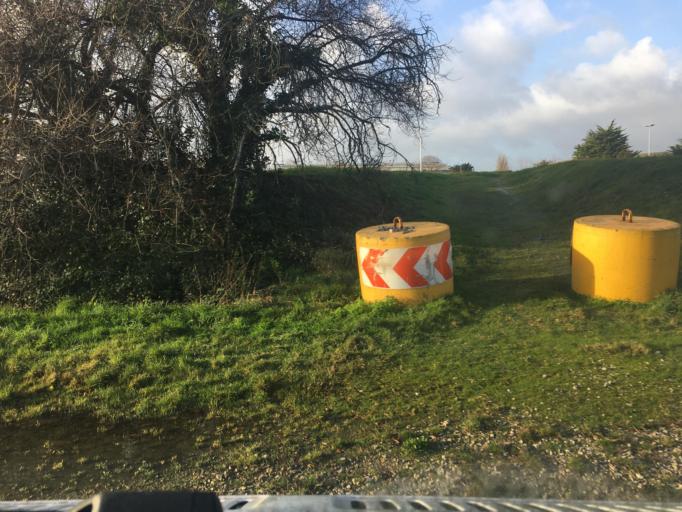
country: FR
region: Lower Normandy
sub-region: Departement de la Manche
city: Equeurdreville-Hainneville
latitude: 49.6495
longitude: -1.6433
